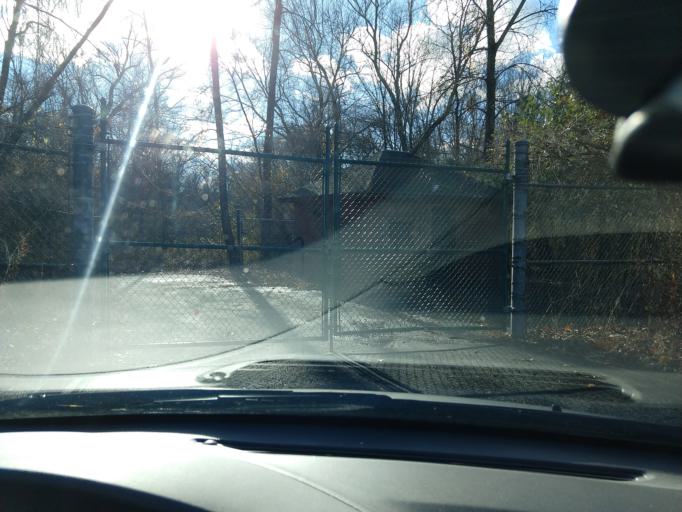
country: US
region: Massachusetts
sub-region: Middlesex County
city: Bedford
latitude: 42.5154
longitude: -71.2626
